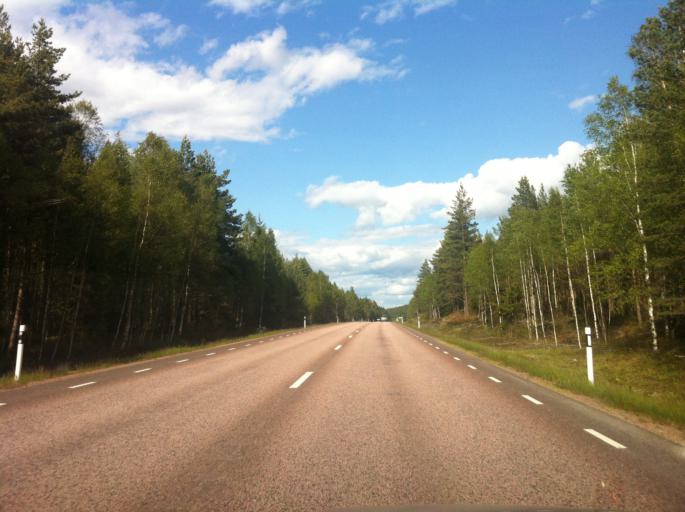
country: SE
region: Vaermland
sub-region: Kristinehamns Kommun
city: Kristinehamn
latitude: 59.3519
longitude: 14.1420
